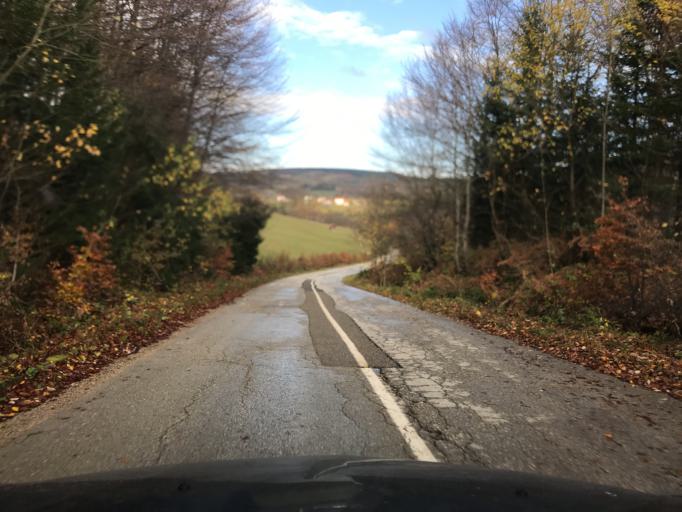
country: BA
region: Republika Srpska
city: Zivinice
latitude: 44.5217
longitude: 17.3546
